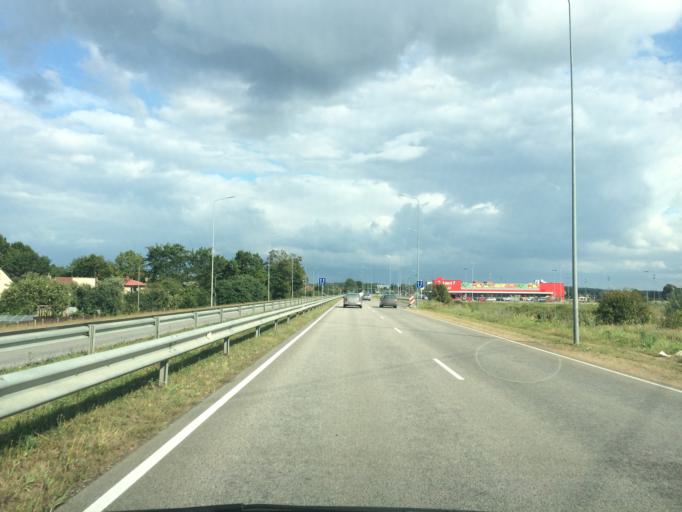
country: LV
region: Ogre
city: Ogre
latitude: 56.8184
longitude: 24.5708
